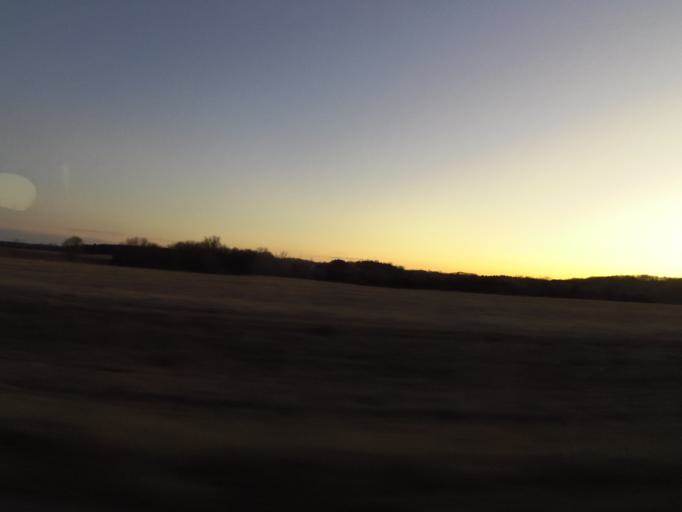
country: US
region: Minnesota
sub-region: Washington County
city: Lake Saint Croix Beach
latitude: 44.9310
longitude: -92.6911
